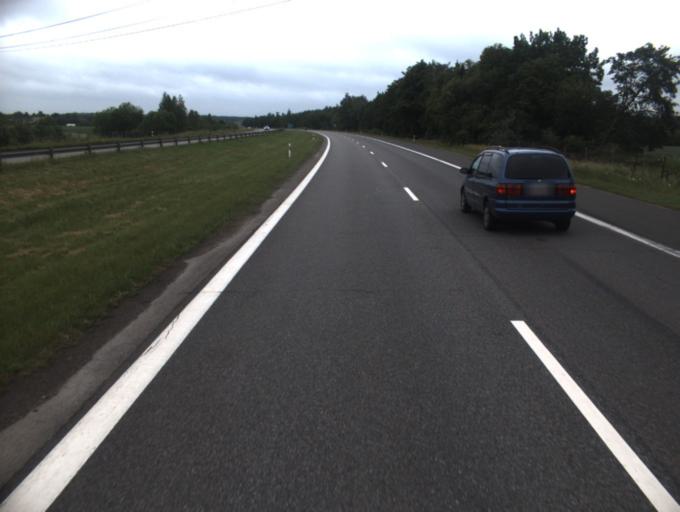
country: LT
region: Kauno apskritis
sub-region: Kaunas
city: Sargenai
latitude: 55.0872
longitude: 23.8112
